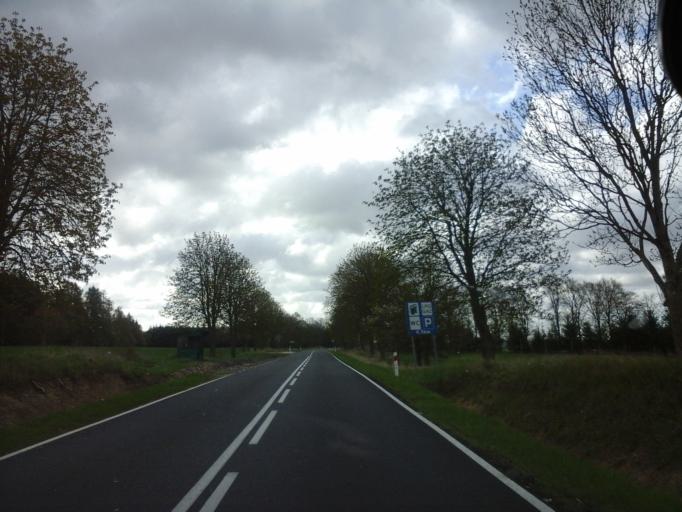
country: PL
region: West Pomeranian Voivodeship
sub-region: Powiat choszczenski
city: Bierzwnik
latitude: 53.0671
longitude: 15.6586
